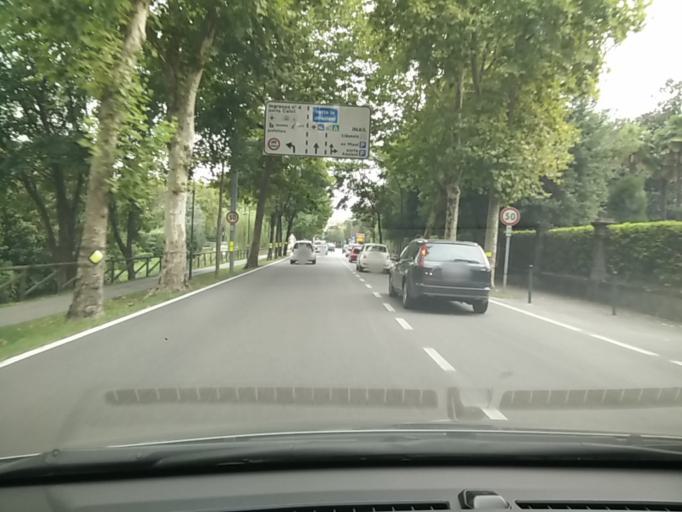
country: IT
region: Veneto
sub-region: Provincia di Treviso
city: Treviso
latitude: 45.6648
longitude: 12.2351
